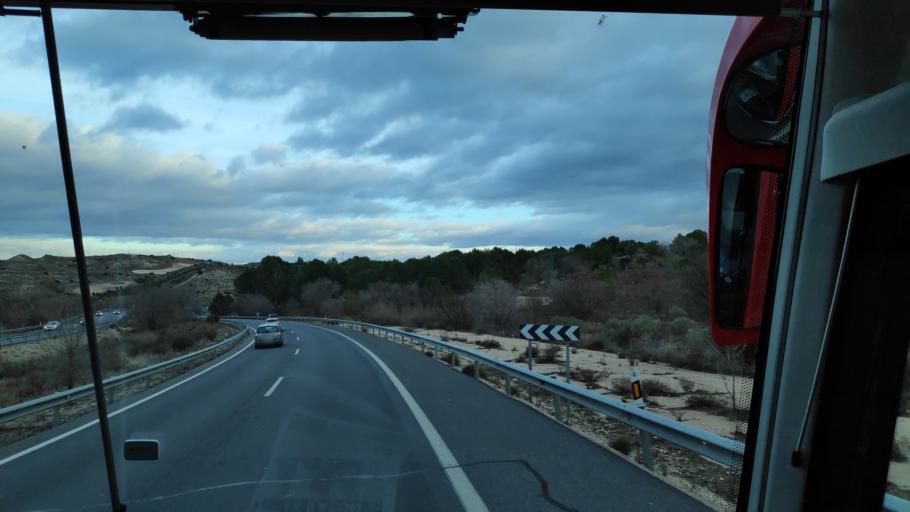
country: ES
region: Madrid
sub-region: Provincia de Madrid
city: Villarejo de Salvanes
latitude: 40.1481
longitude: -3.2265
